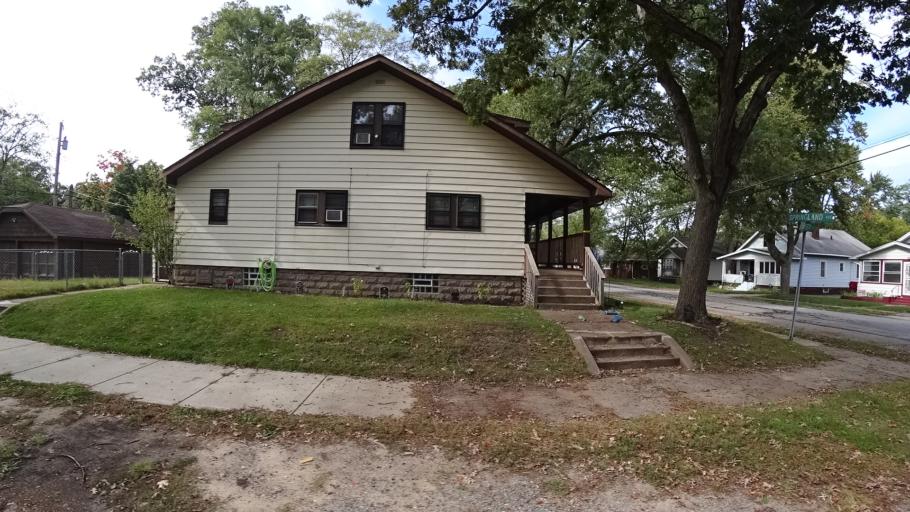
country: US
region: Indiana
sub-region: LaPorte County
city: Michigan City
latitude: 41.7168
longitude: -86.8803
